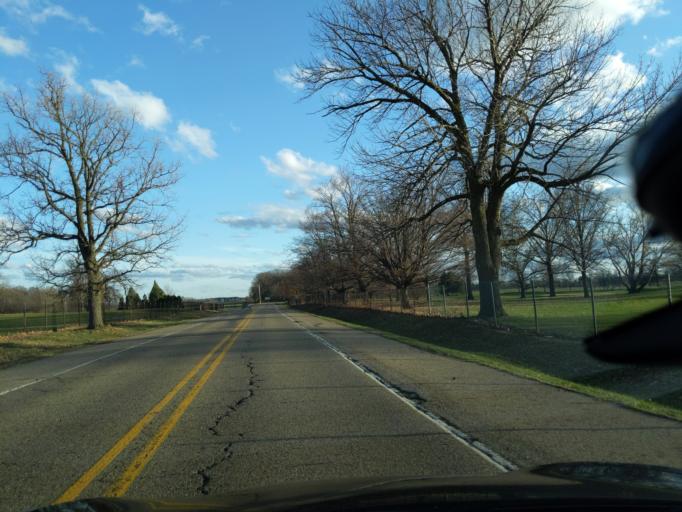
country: US
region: Michigan
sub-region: Ingham County
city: East Lansing
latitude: 42.7066
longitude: -84.4939
